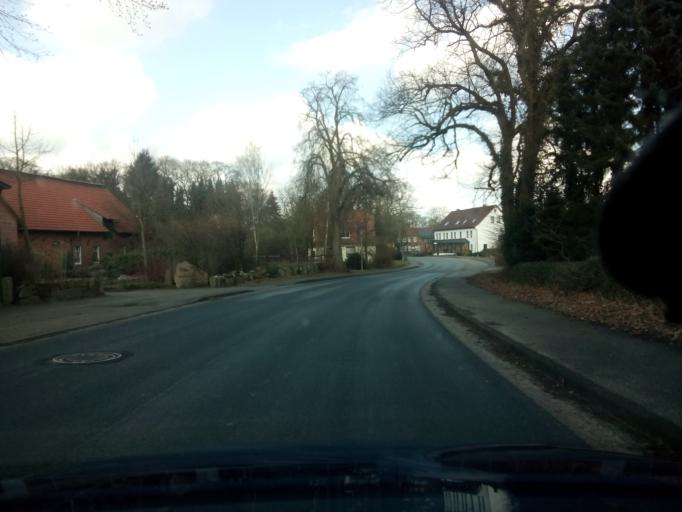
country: DE
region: Lower Saxony
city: Basdahl
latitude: 53.4410
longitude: 8.9970
